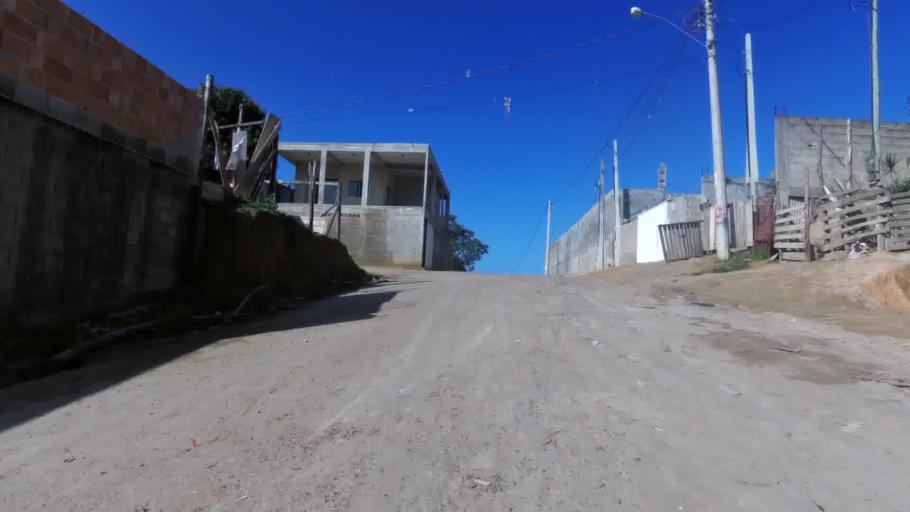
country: BR
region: Espirito Santo
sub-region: Piuma
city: Piuma
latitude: -20.8215
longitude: -40.6221
